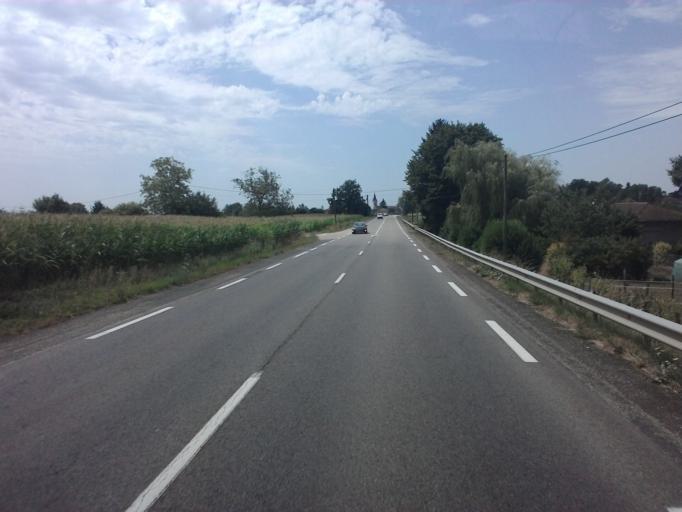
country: FR
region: Rhone-Alpes
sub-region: Departement de l'Ain
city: Coligny
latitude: 46.3518
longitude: 5.3255
